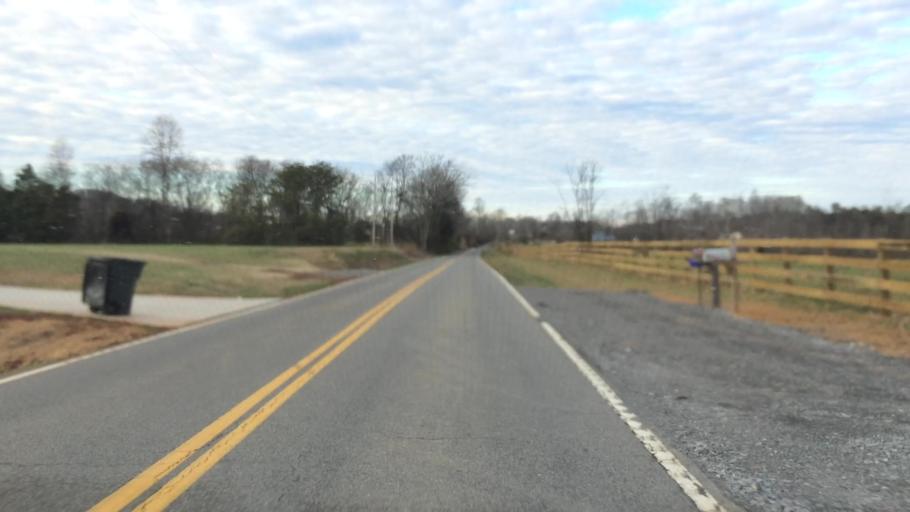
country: US
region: Tennessee
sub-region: McMinn County
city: Athens
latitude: 35.4737
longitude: -84.5350
